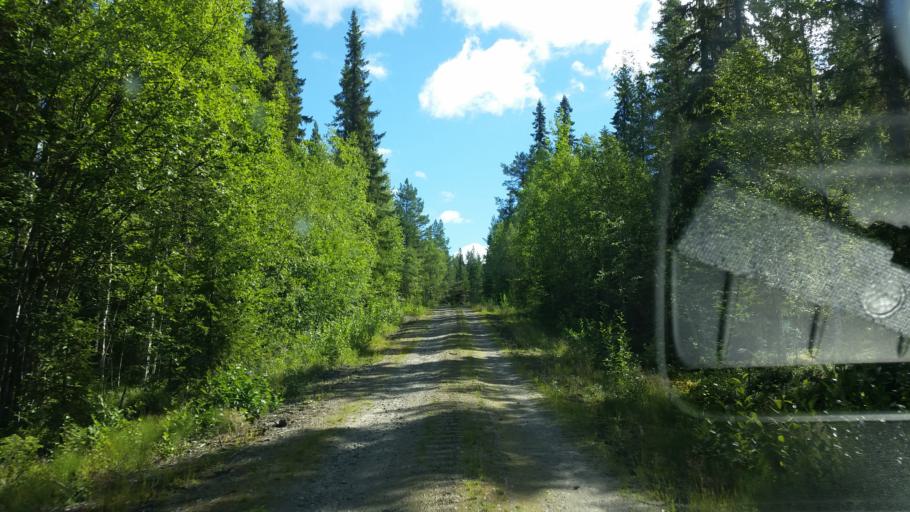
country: SE
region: Vaesternorrland
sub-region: Ange Kommun
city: Ange
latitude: 62.2324
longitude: 15.7330
